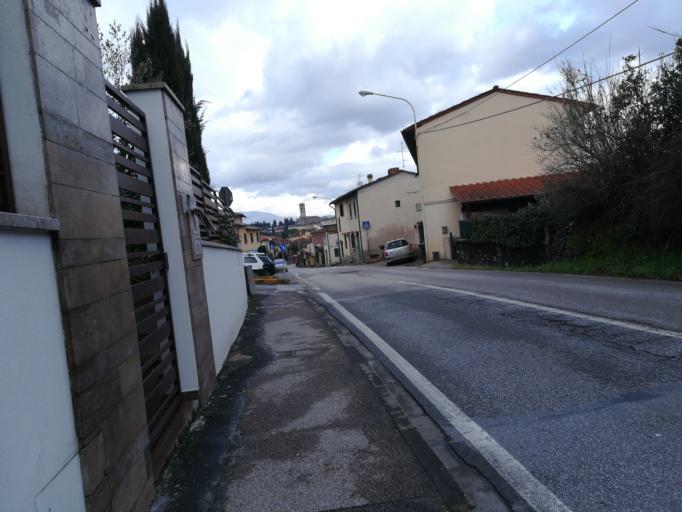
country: IT
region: Tuscany
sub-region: Provincia di Prato
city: Poggio A Caiano
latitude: 43.8104
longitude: 11.0523
